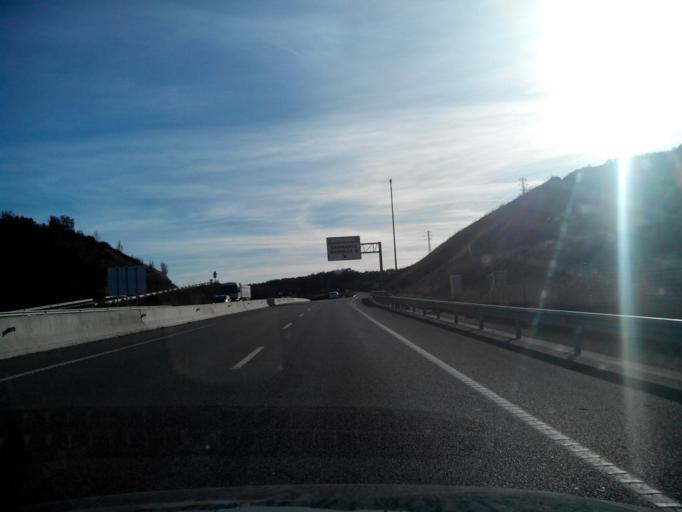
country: ES
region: Catalonia
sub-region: Provincia de Barcelona
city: Gironella
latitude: 42.0359
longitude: 1.8743
